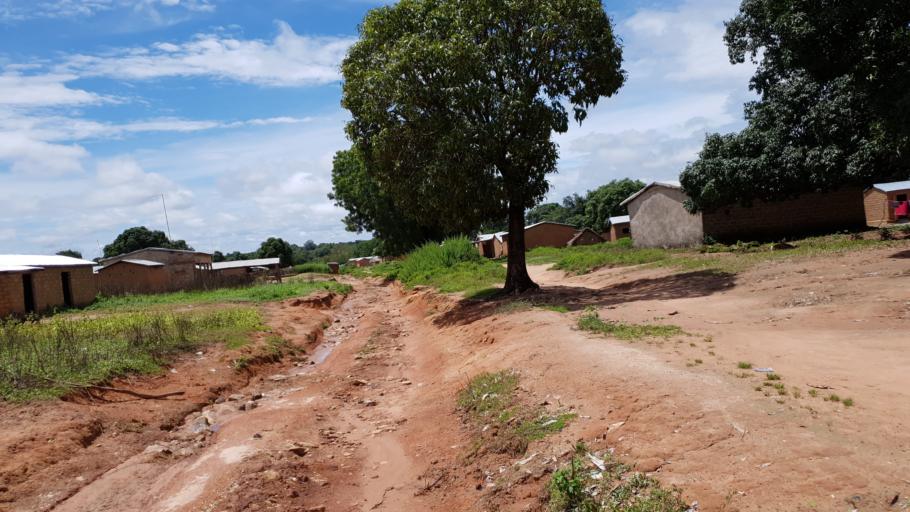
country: CI
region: Savanes
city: Tengrela
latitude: 10.3599
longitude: -6.9191
